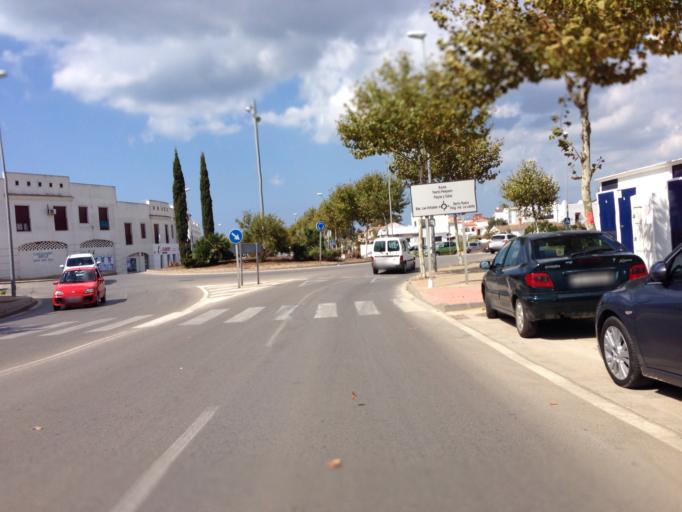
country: ES
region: Andalusia
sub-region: Provincia de Cadiz
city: Conil de la Frontera
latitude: 36.2843
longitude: -6.0849
